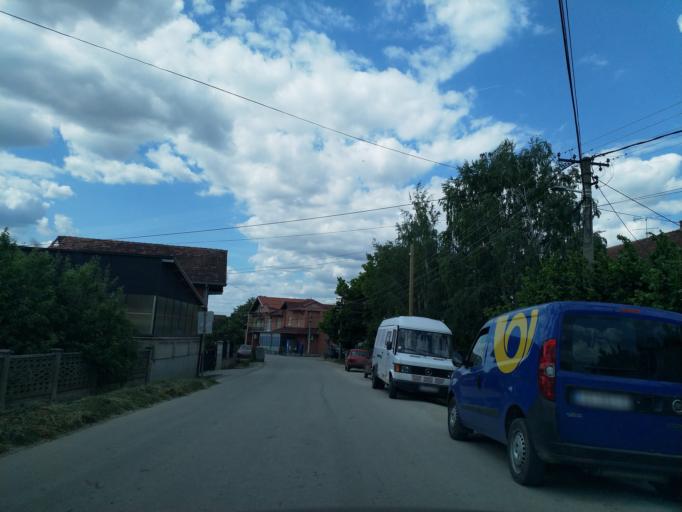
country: RS
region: Central Serbia
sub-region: Pomoravski Okrug
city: Jagodina
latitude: 43.9459
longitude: 21.2963
